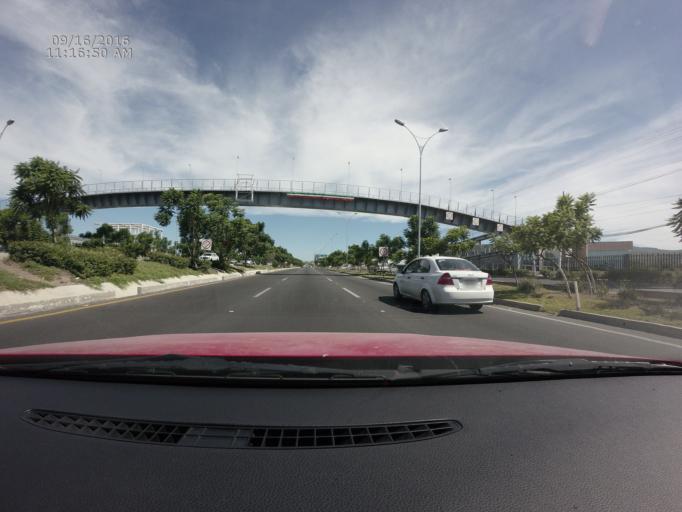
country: MX
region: Queretaro
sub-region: Queretaro
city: El Salitre
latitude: 20.6661
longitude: -100.4332
